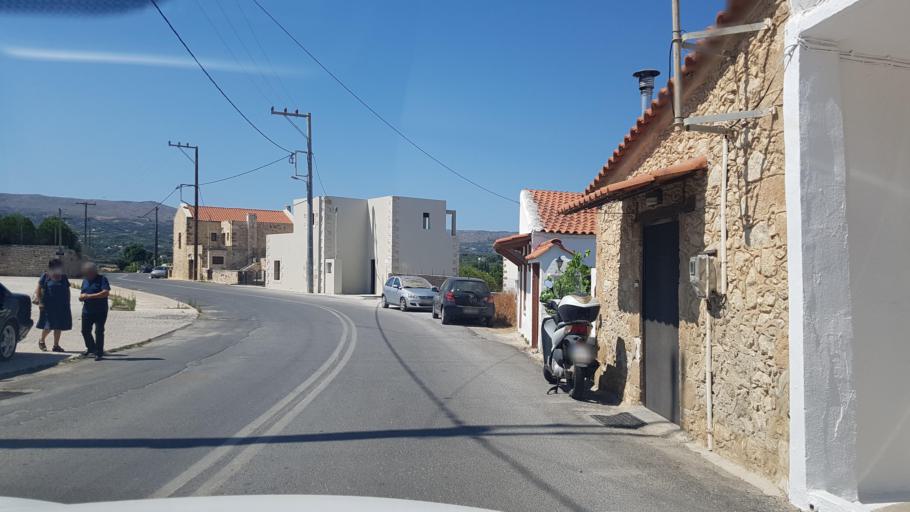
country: GR
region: Crete
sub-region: Nomos Rethymnis
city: Panormos
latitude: 35.3725
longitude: 24.5969
